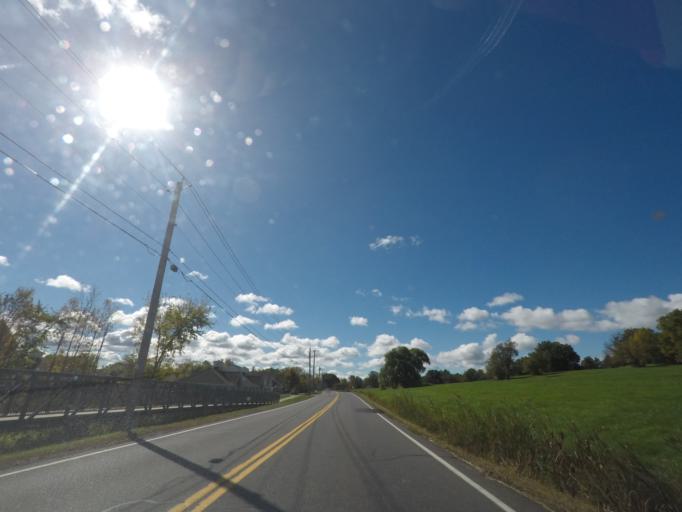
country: US
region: New York
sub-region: Albany County
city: Watervliet
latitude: 42.7321
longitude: -73.7351
